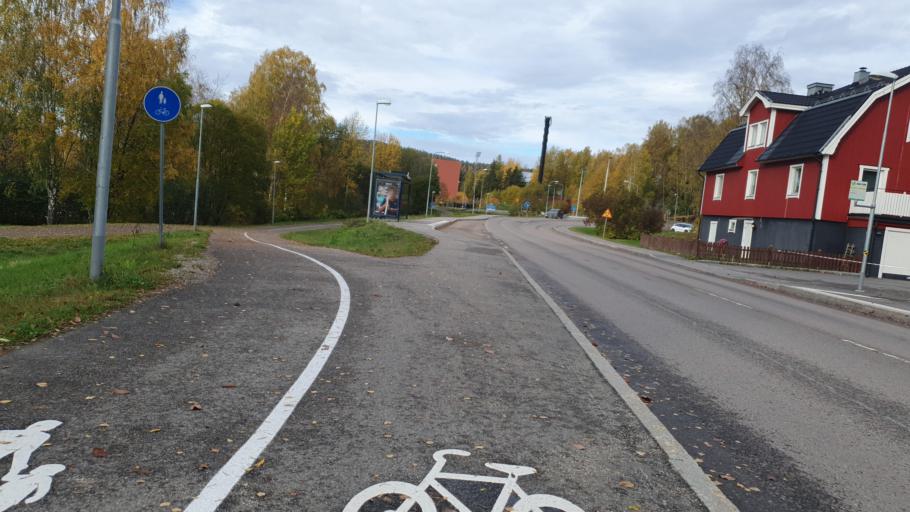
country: SE
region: Vaesternorrland
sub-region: Sundsvalls Kommun
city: Sundsvall
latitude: 62.4107
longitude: 17.2287
